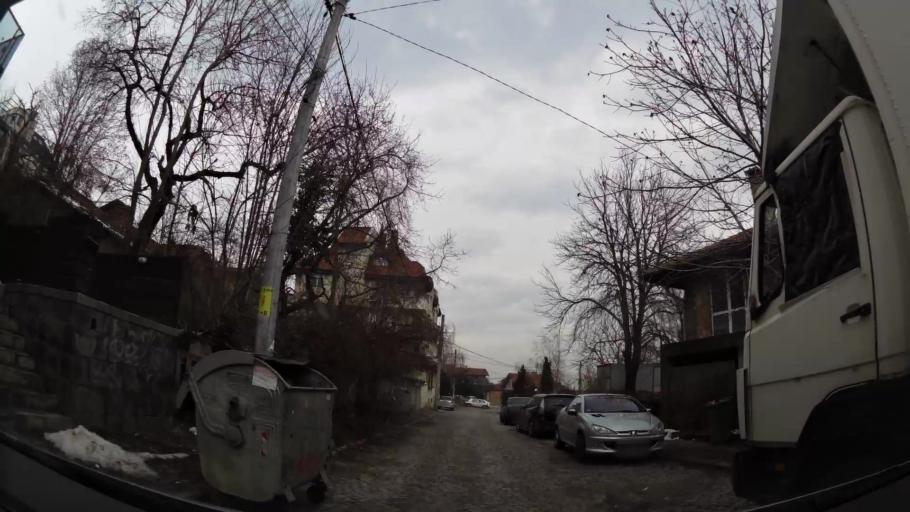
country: BG
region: Sofia-Capital
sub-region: Stolichna Obshtina
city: Sofia
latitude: 42.6636
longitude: 23.2430
